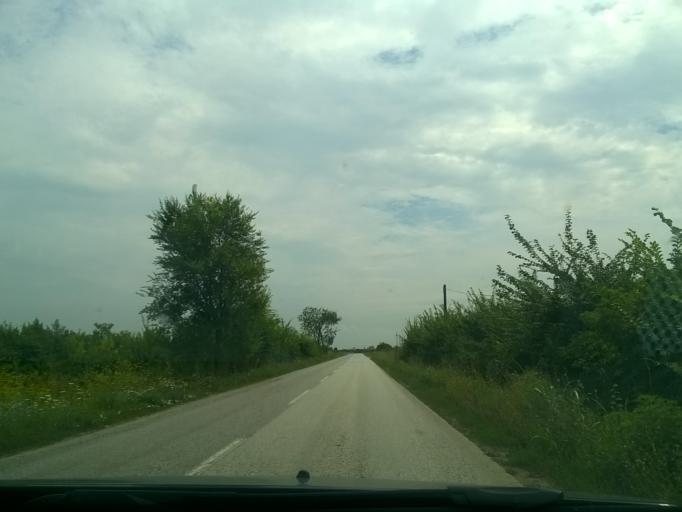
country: RS
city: Boka
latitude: 45.3536
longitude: 20.8401
